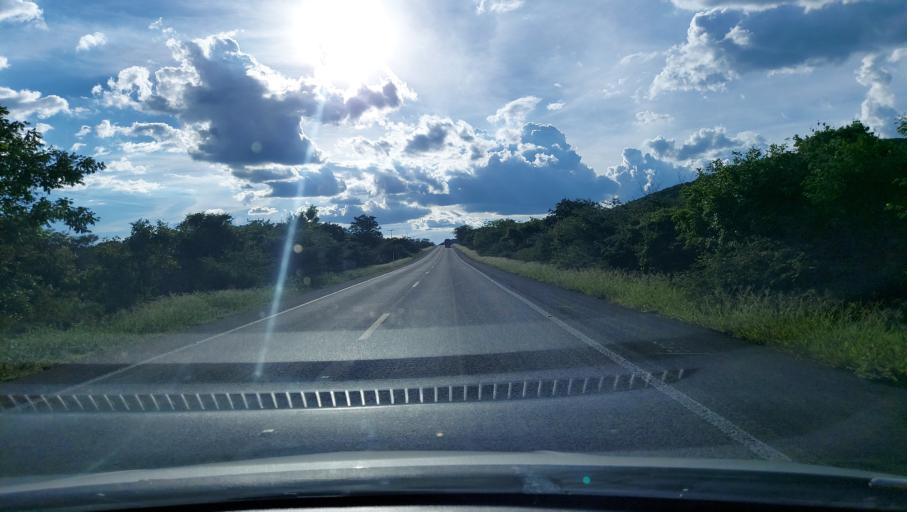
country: BR
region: Bahia
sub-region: Seabra
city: Seabra
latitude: -12.4650
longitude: -42.2556
